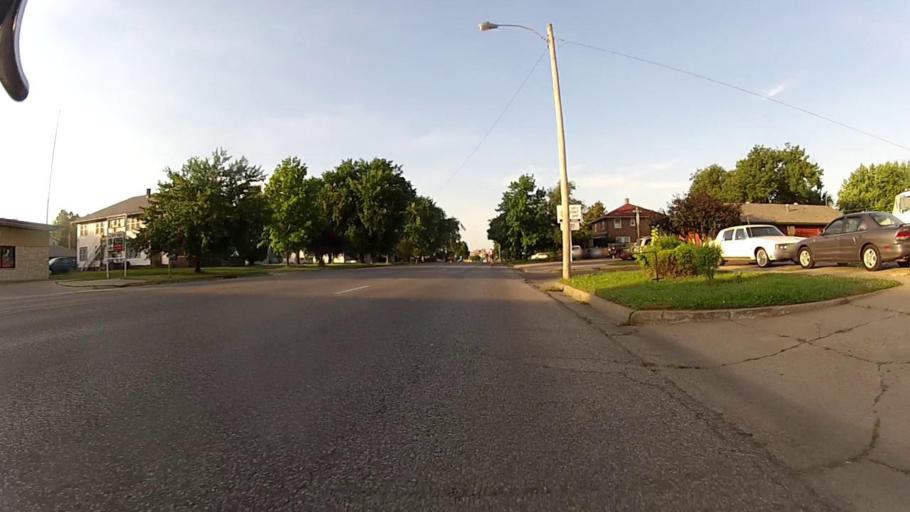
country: US
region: Kansas
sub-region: Cowley County
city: Arkansas City
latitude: 37.0725
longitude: -97.0391
